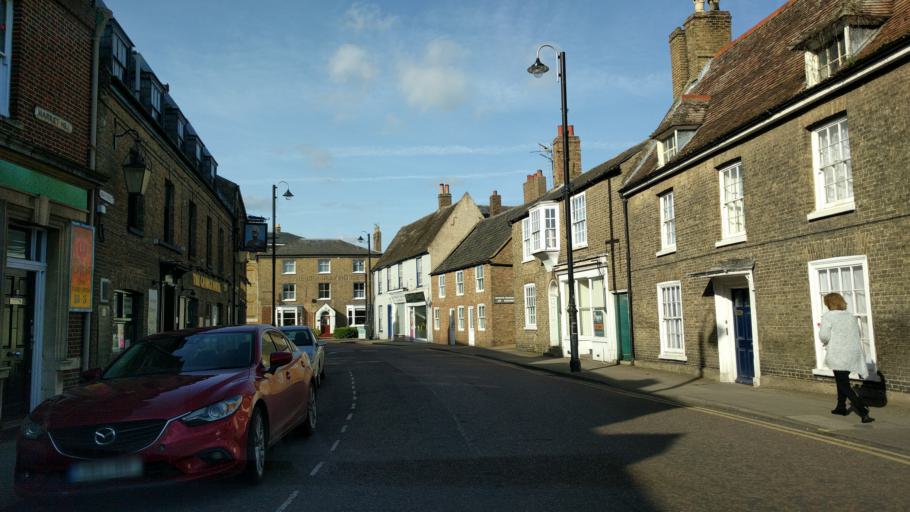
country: GB
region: England
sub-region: Cambridgeshire
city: Chatteris
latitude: 52.4548
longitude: 0.0500
